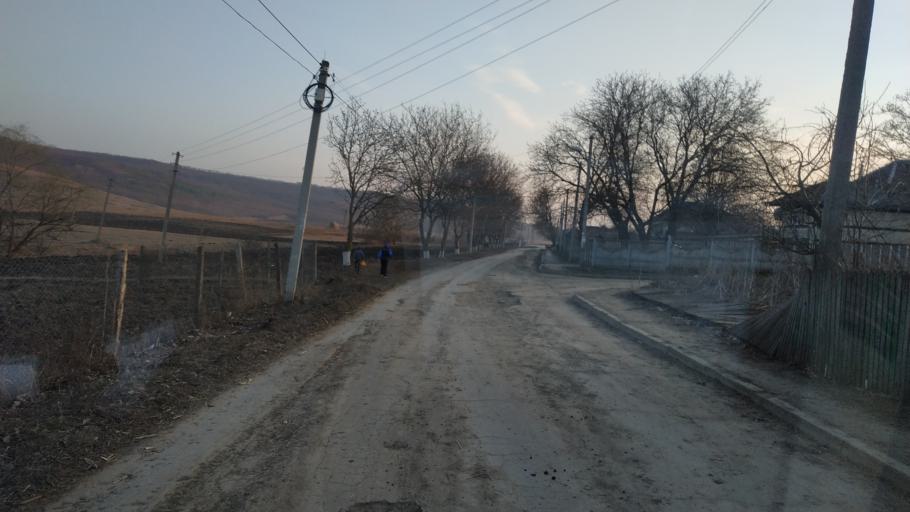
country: MD
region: Hincesti
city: Dancu
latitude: 46.7072
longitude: 28.3451
